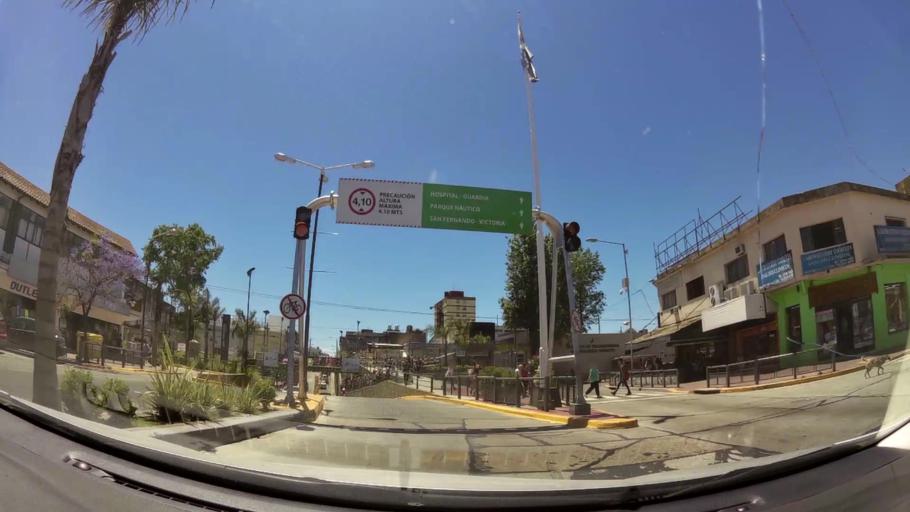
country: AR
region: Buenos Aires
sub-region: Partido de Tigre
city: Tigre
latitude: -34.4505
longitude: -58.5519
